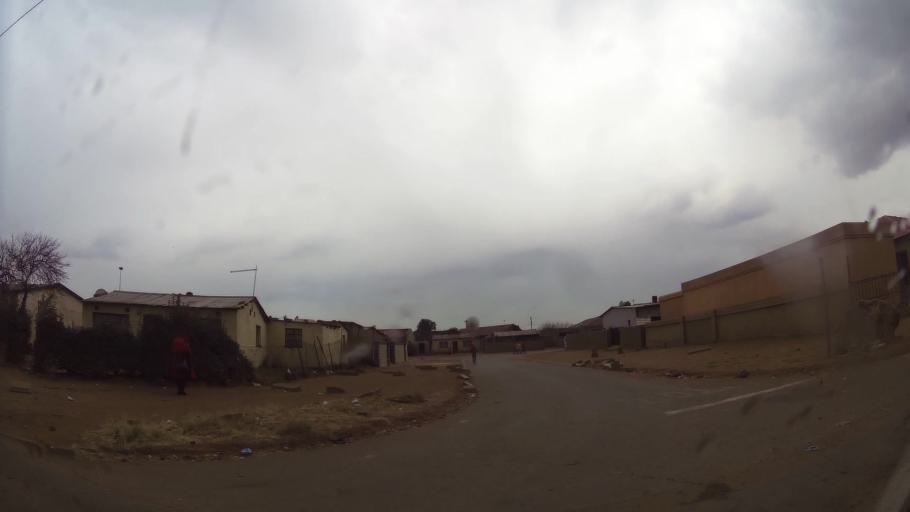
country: ZA
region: Gauteng
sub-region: Ekurhuleni Metropolitan Municipality
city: Germiston
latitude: -26.3404
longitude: 28.1440
